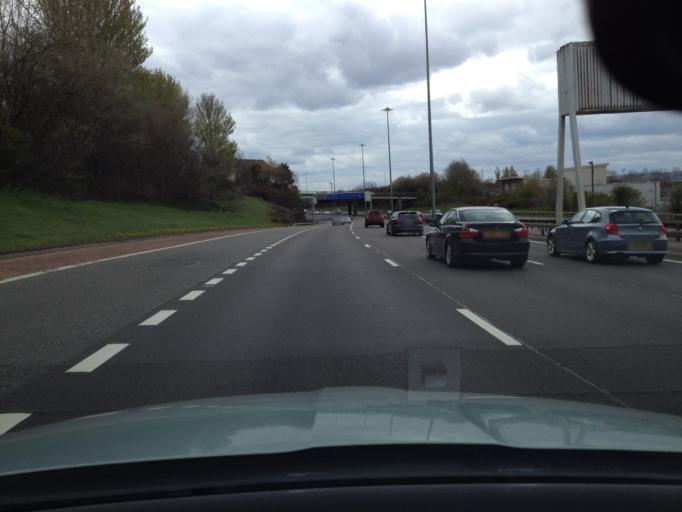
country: GB
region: Scotland
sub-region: North Lanarkshire
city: Stepps
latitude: 55.8704
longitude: -4.1764
